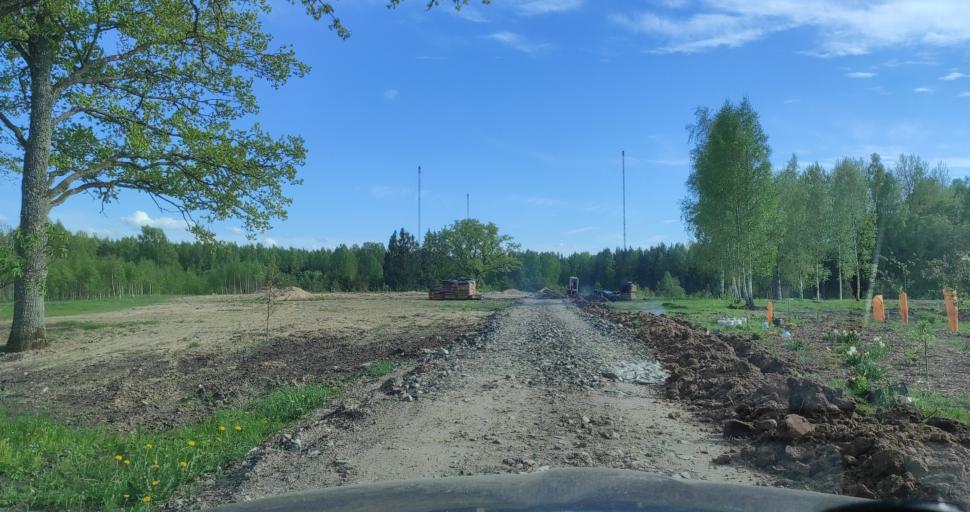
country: LV
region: Kuldigas Rajons
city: Kuldiga
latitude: 56.9481
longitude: 21.9181
